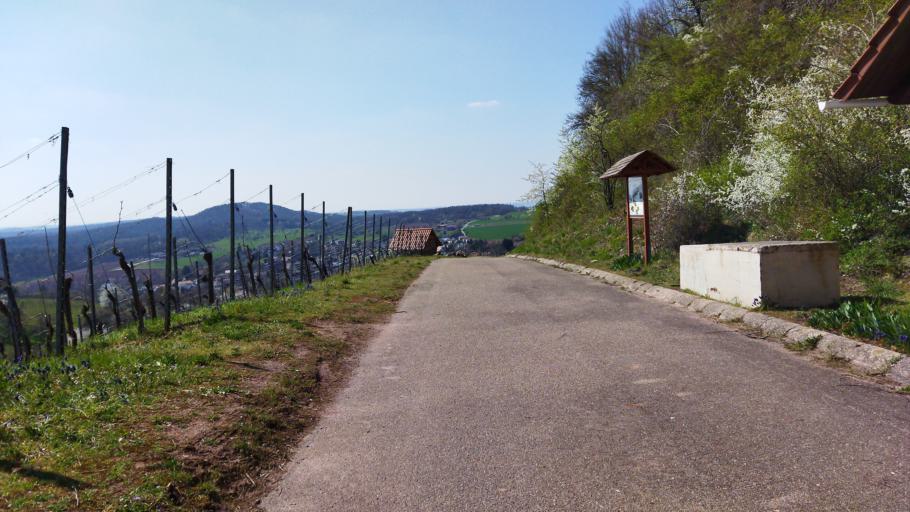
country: DE
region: Baden-Wuerttemberg
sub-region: Karlsruhe Region
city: Sternenfels
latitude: 49.0272
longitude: 8.8652
